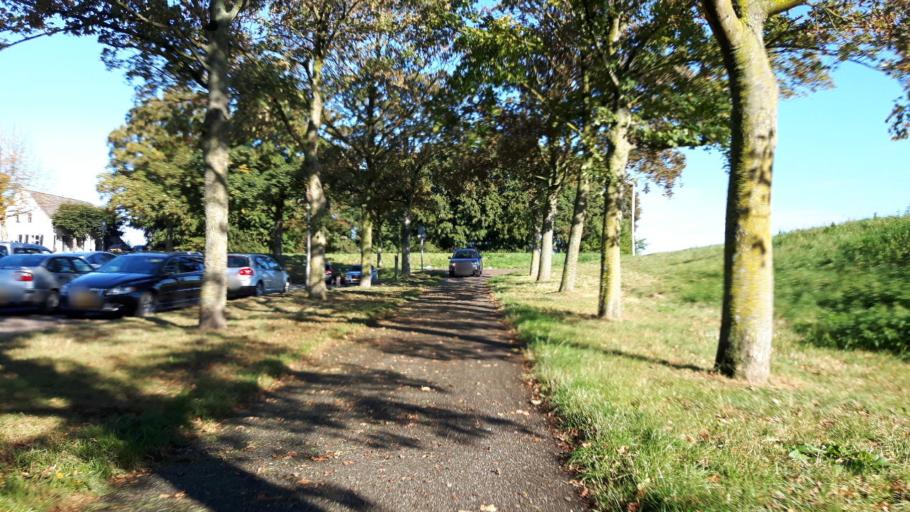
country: NL
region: Utrecht
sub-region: Gemeente Vianen
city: Vianen
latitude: 51.9956
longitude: 5.0965
